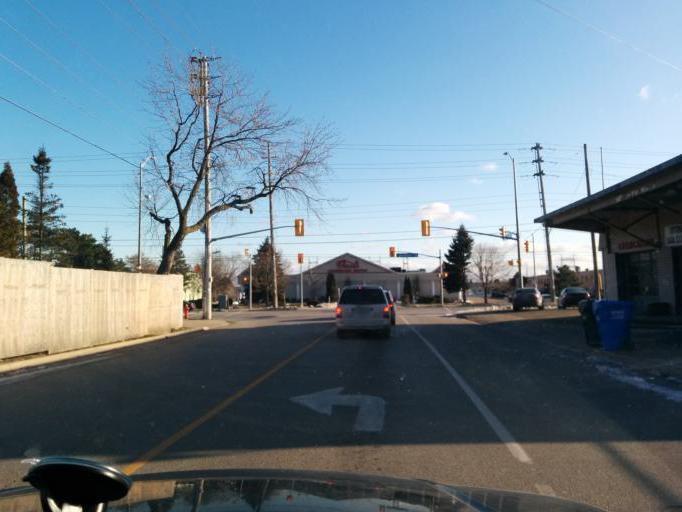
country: CA
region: Ontario
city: Etobicoke
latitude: 43.5773
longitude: -79.5592
